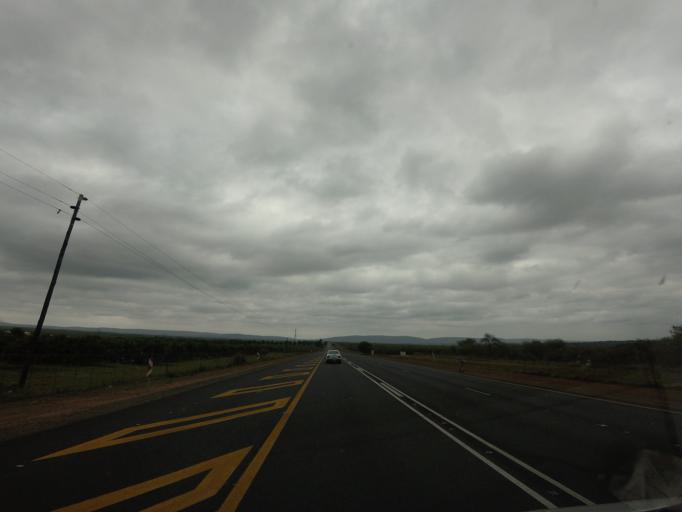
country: ZA
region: Mpumalanga
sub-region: Ehlanzeni District
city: Komatipoort
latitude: -25.4394
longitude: 31.8650
